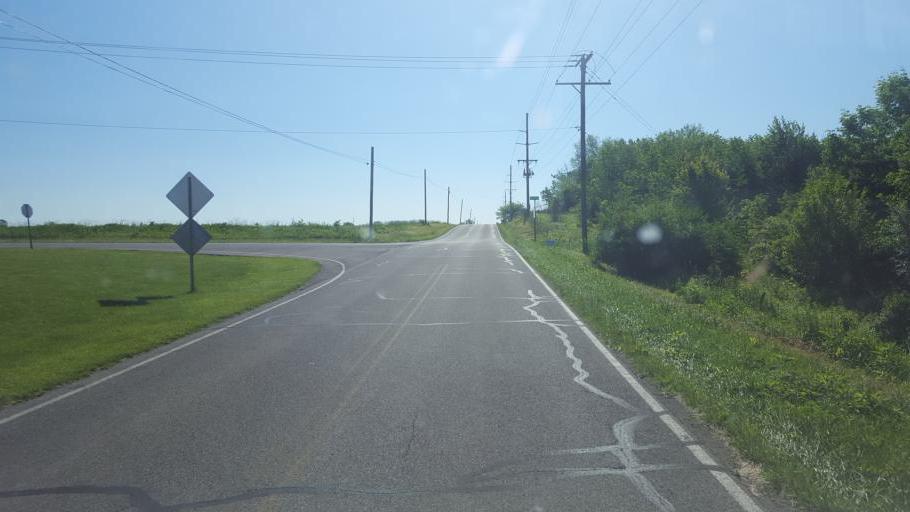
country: US
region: Ohio
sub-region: Crawford County
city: Crestline
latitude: 40.7696
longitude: -82.7382
